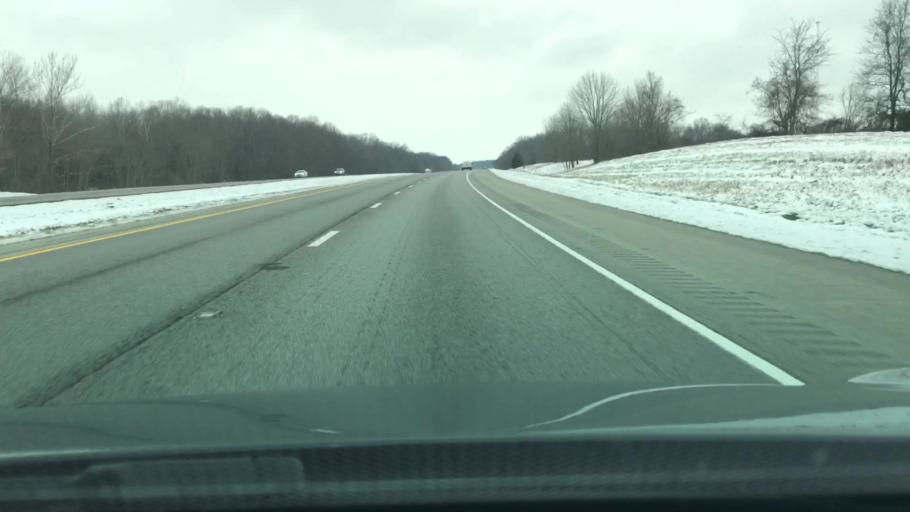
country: US
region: Illinois
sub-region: Clinton County
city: Wamac
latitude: 38.3652
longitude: -89.0862
